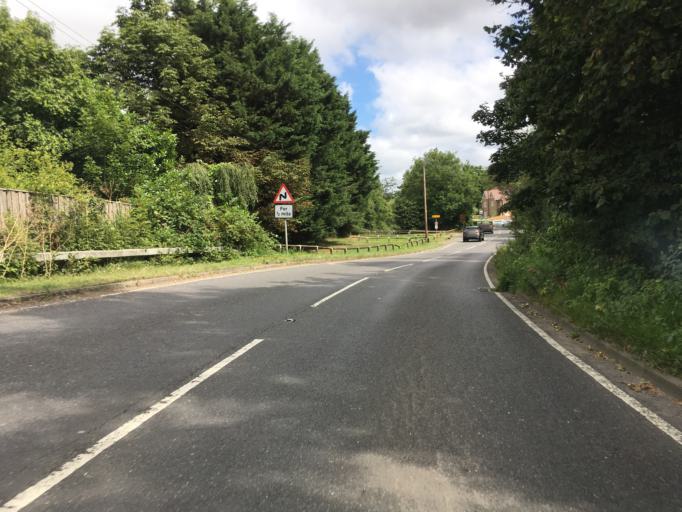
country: GB
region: England
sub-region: Kent
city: Marden
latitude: 51.1090
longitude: 0.4382
